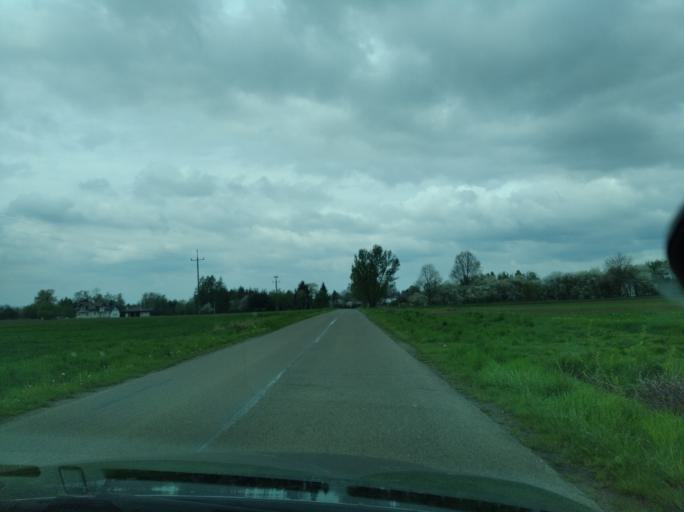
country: PL
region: Subcarpathian Voivodeship
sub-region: Powiat brzozowski
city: Gorki
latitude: 49.6180
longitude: 22.0252
